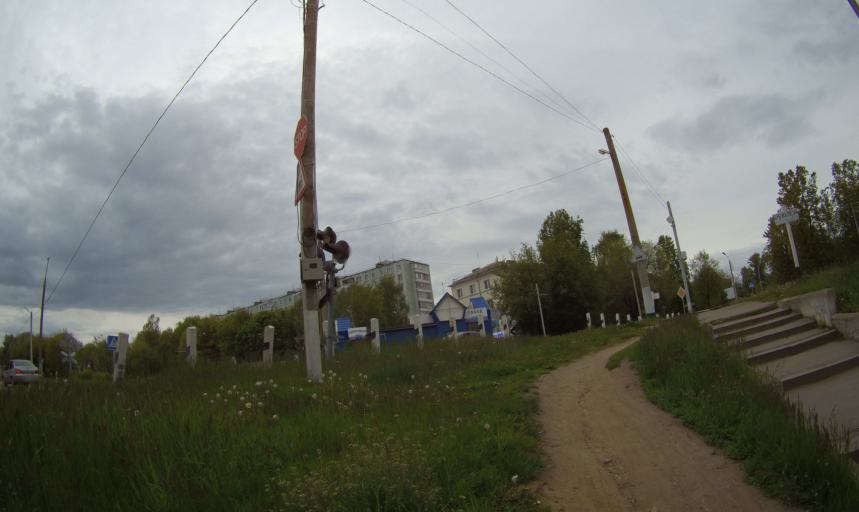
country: RU
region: Moskovskaya
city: Kolomna
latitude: 55.0745
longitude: 38.8014
